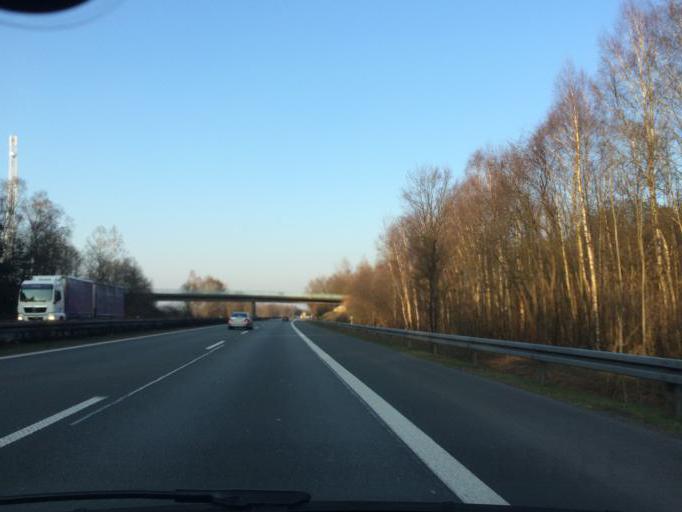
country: DE
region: North Rhine-Westphalia
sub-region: Regierungsbezirk Munster
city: Haltern
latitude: 51.8094
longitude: 7.1956
